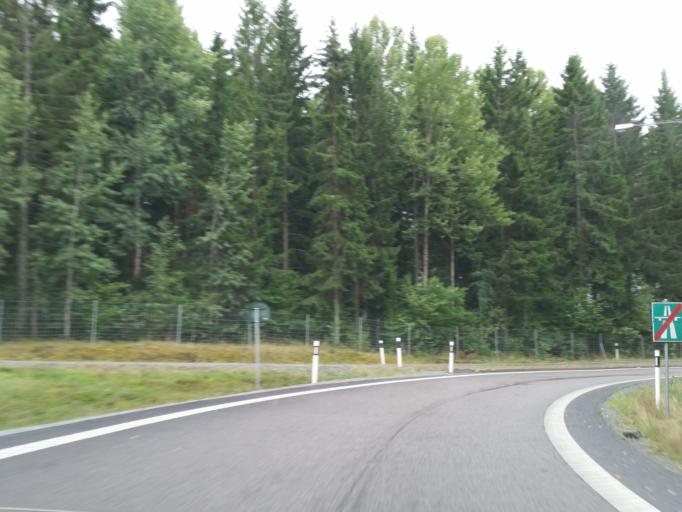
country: SE
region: Uppsala
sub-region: Enkopings Kommun
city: Dalby
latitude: 59.6190
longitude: 17.3931
